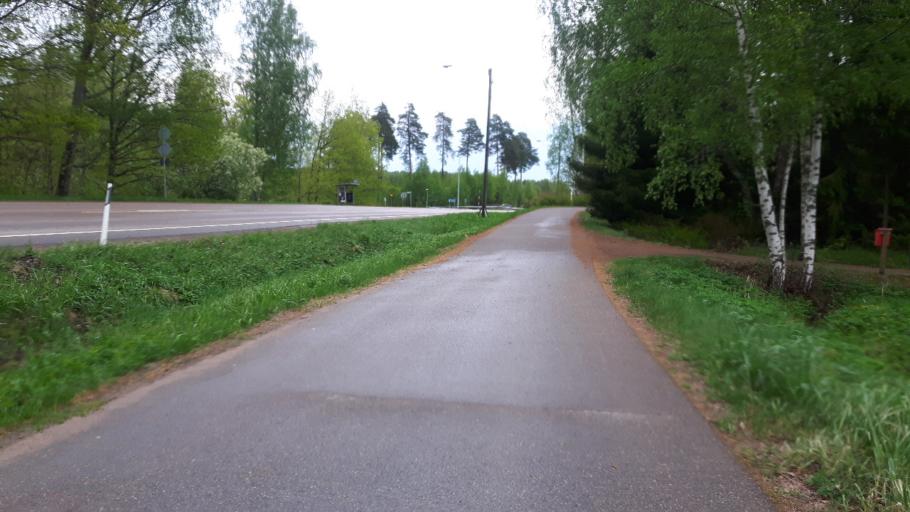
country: FI
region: Kymenlaakso
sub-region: Kotka-Hamina
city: Hamina
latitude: 60.5659
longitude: 27.1026
